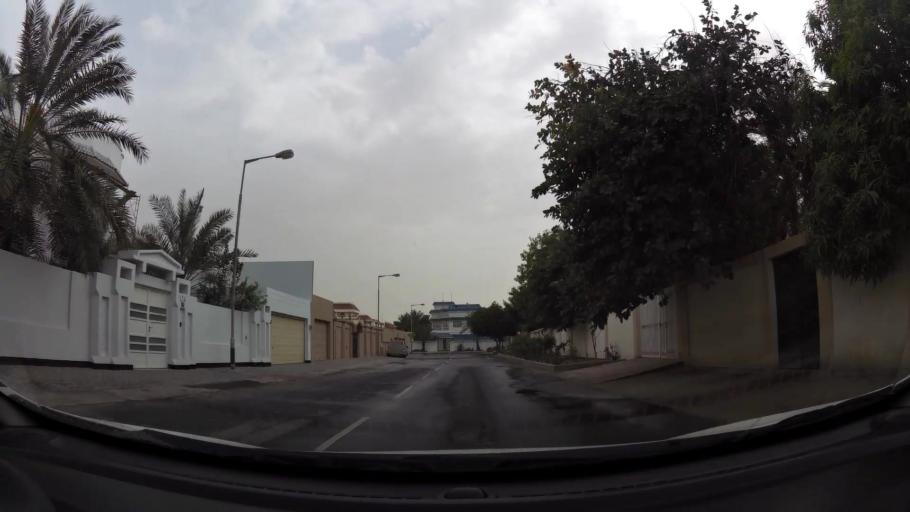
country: BH
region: Northern
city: Ar Rifa'
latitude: 26.1332
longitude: 50.5452
